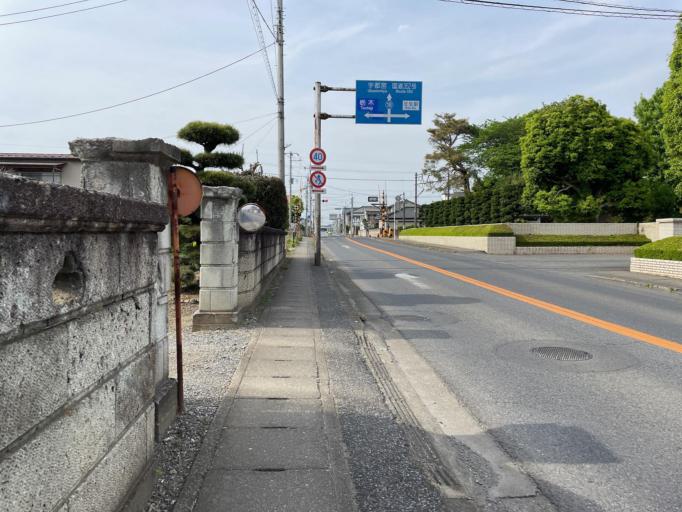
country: JP
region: Tochigi
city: Mibu
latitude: 36.4194
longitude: 139.8025
